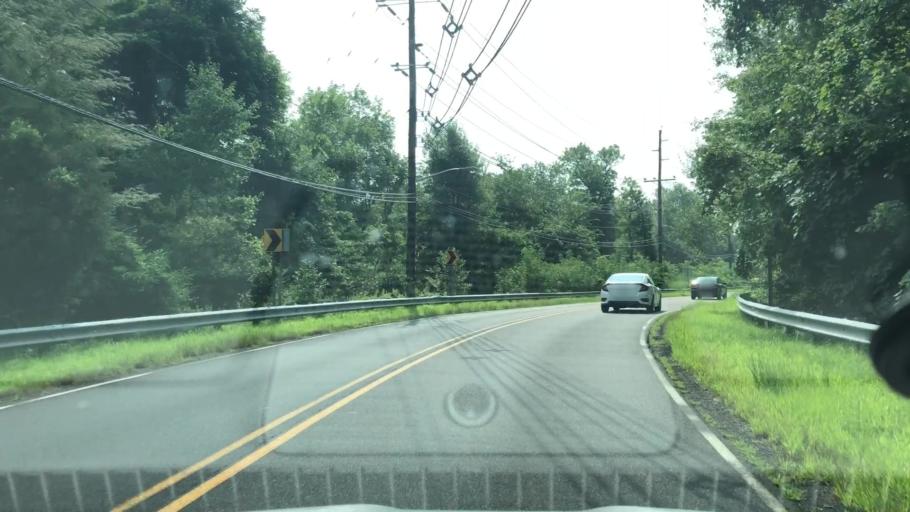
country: US
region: New Jersey
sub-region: Mercer County
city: Lawrenceville
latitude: 40.3046
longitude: -74.6908
